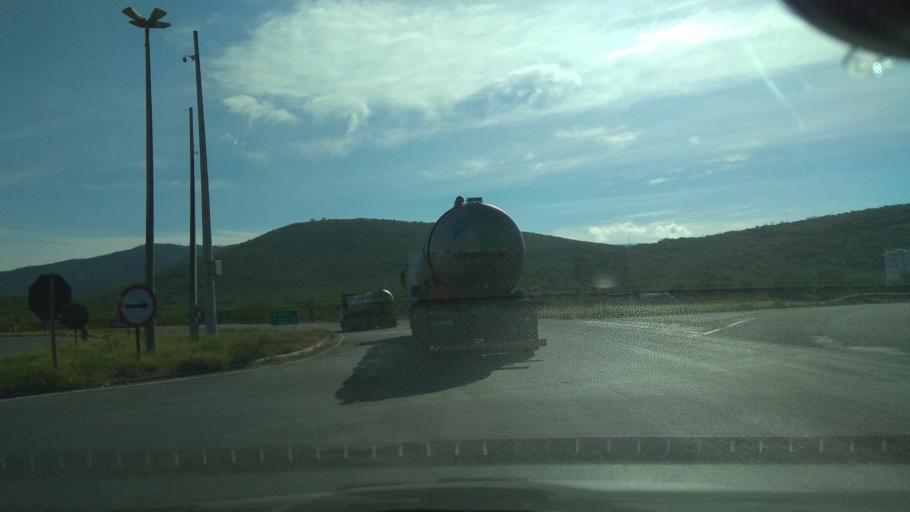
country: BR
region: Bahia
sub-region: Jequie
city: Jequie
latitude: -13.8358
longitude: -40.1061
